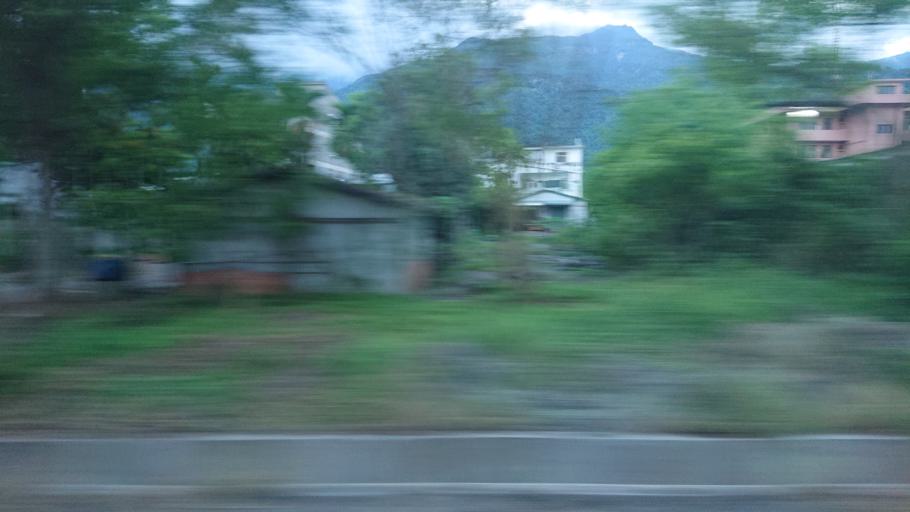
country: TW
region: Taiwan
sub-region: Taitung
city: Taitung
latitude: 23.0496
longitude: 121.1657
